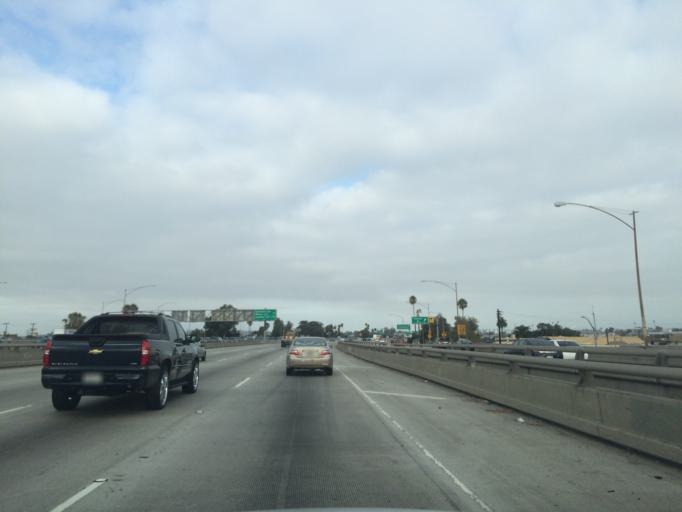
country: US
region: California
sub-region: Los Angeles County
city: Los Angeles
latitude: 34.0375
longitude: -118.2830
